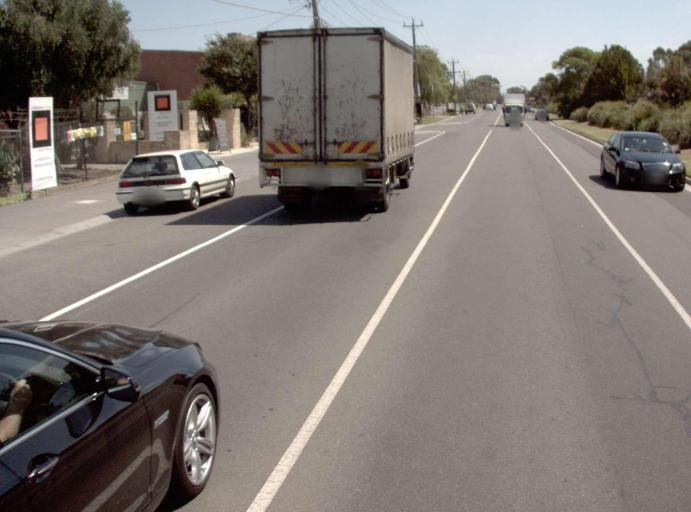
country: AU
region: Victoria
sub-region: Kingston
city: Mordialloc
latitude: -38.0077
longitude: 145.1021
